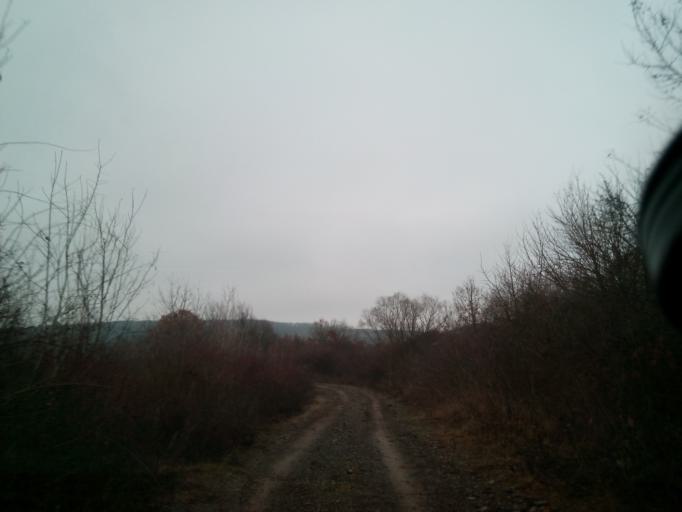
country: SK
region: Kosicky
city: Kosice
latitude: 48.6904
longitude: 21.4450
